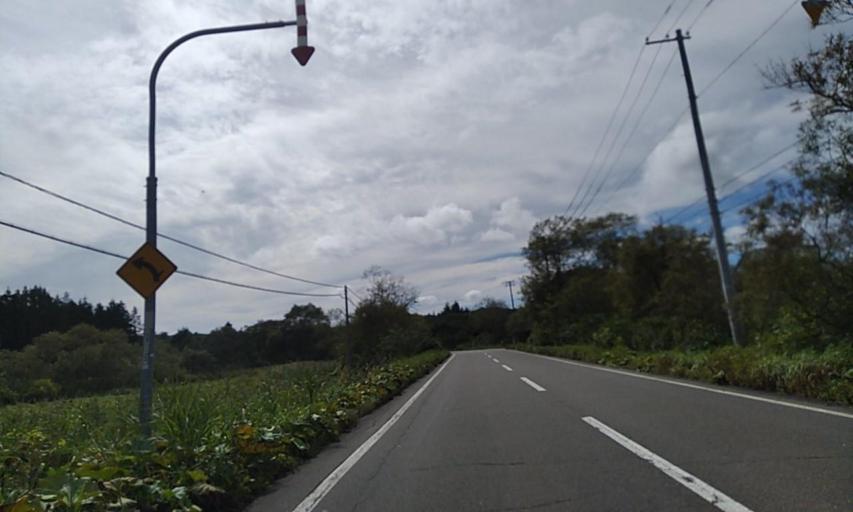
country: JP
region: Hokkaido
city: Kushiro
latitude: 42.8453
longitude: 143.8439
